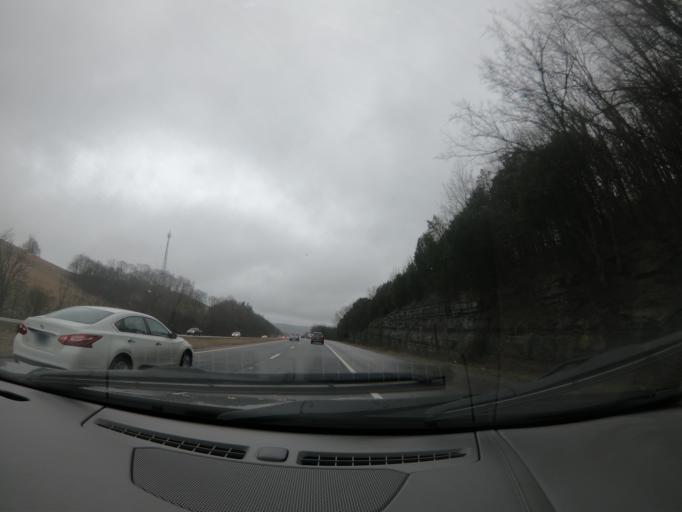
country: US
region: Tennessee
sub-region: Rutherford County
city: Plainview
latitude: 35.5903
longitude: -86.2382
